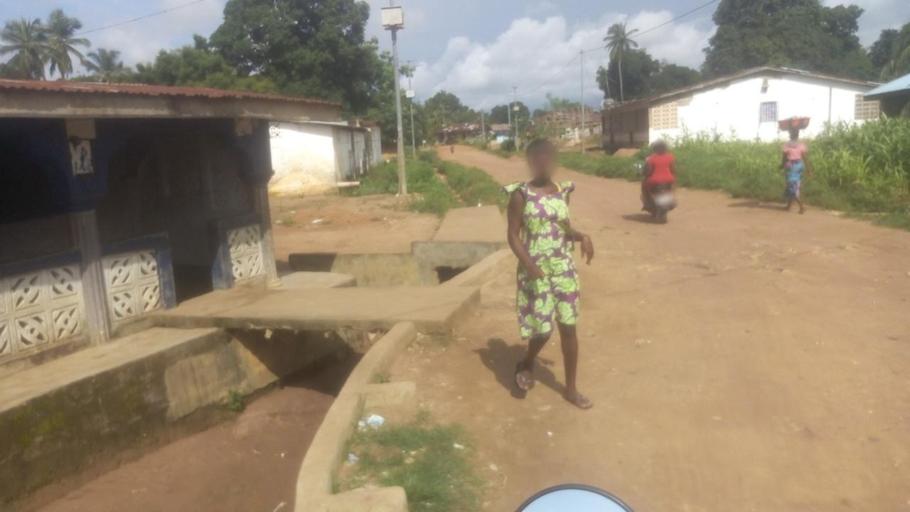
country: SL
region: Northern Province
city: Masoyila
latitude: 8.6116
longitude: -13.1928
